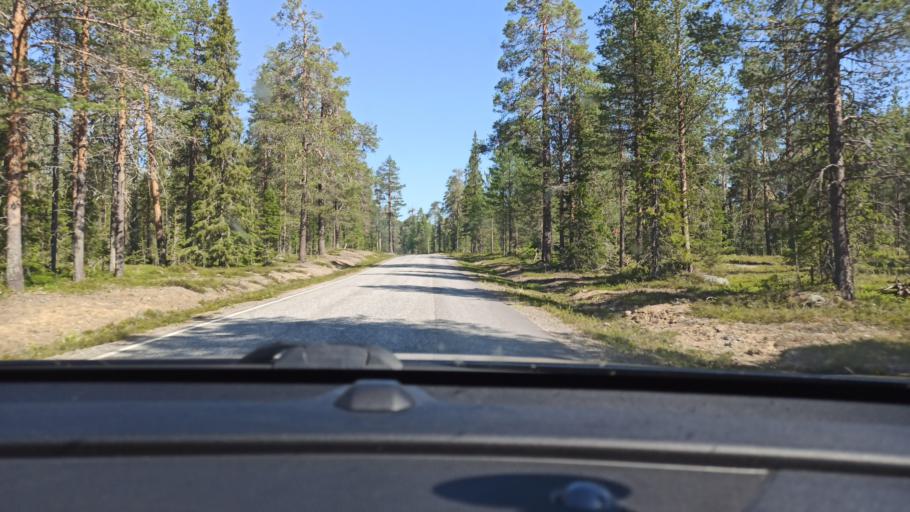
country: FI
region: Lapland
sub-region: Tunturi-Lappi
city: Kolari
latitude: 67.6580
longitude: 24.1652
